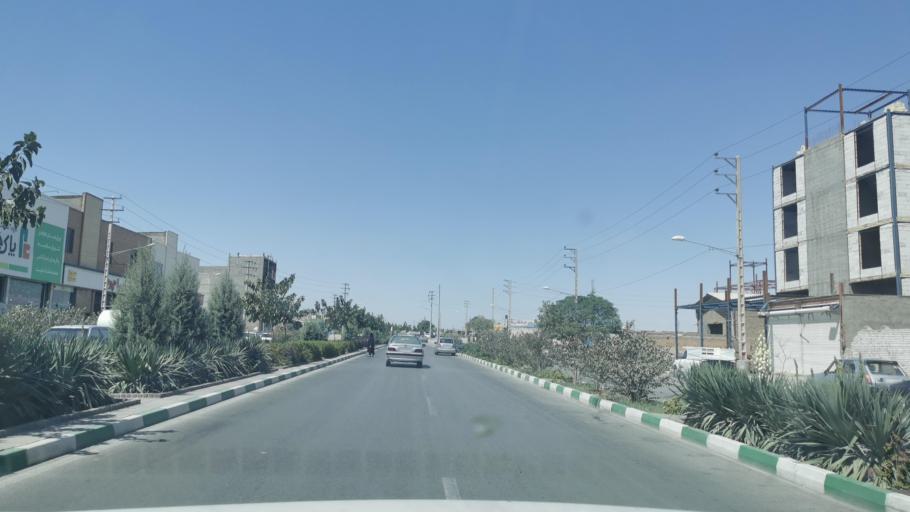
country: IR
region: Razavi Khorasan
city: Mashhad
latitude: 36.3517
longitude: 59.5737
